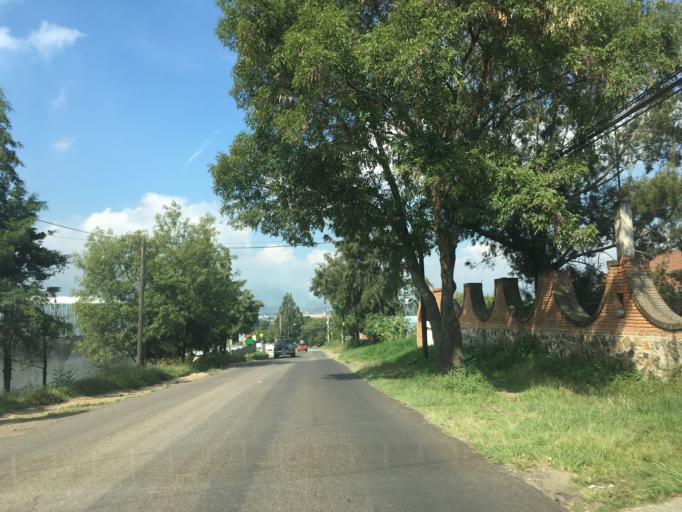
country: MX
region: Michoacan
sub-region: Morelia
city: Morelos
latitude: 19.6493
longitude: -101.2451
